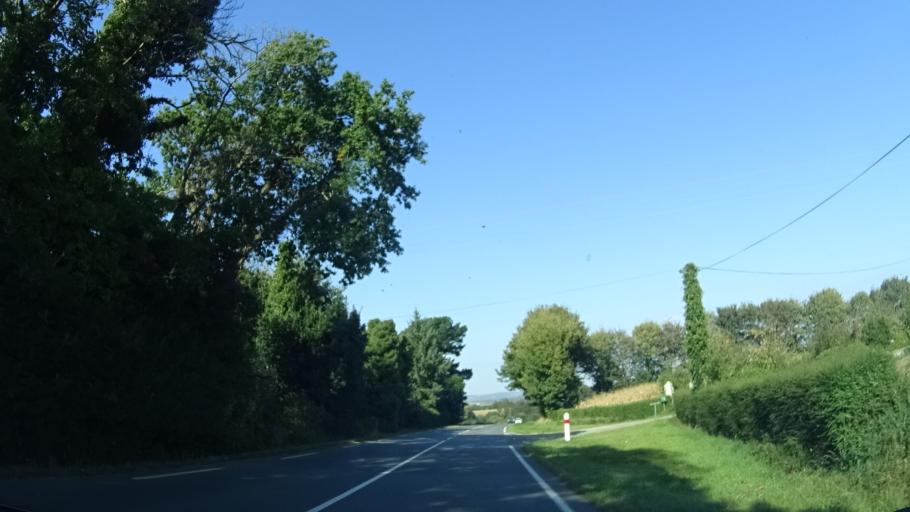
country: FR
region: Brittany
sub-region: Departement du Finistere
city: Plonevez-Porzay
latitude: 48.0979
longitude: -4.2555
